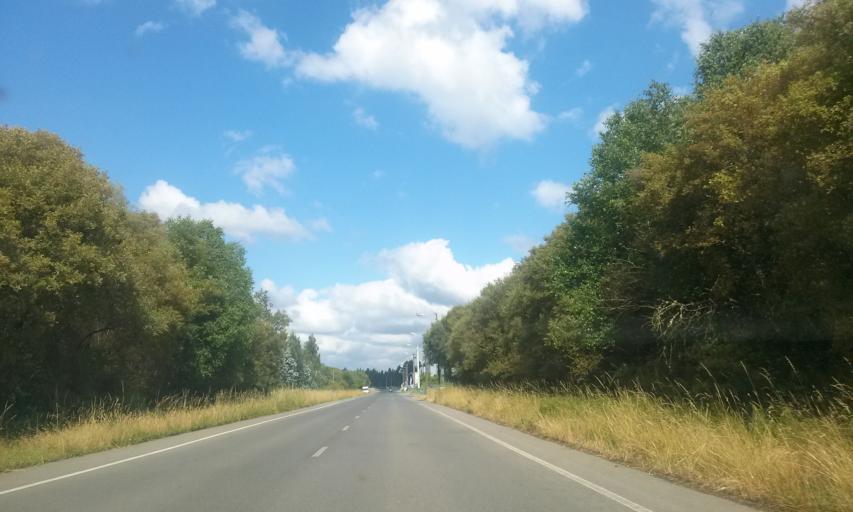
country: ES
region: Galicia
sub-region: Provincia de Lugo
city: Rabade
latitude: 43.1172
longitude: -7.6354
